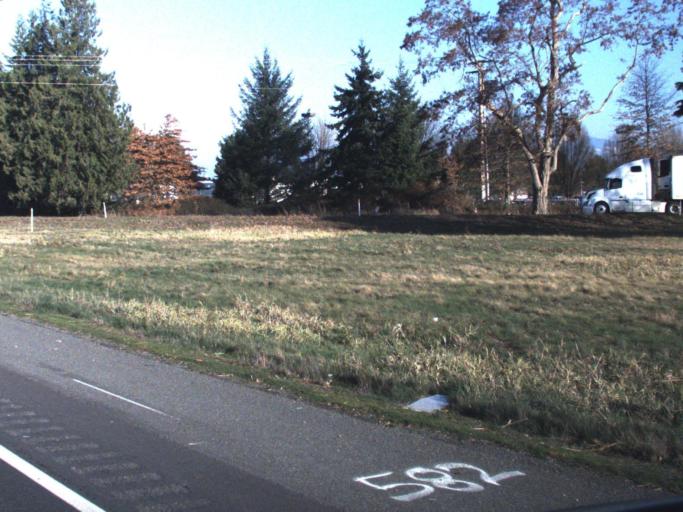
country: US
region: Washington
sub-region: Skagit County
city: Burlington
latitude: 48.4533
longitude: -122.3412
